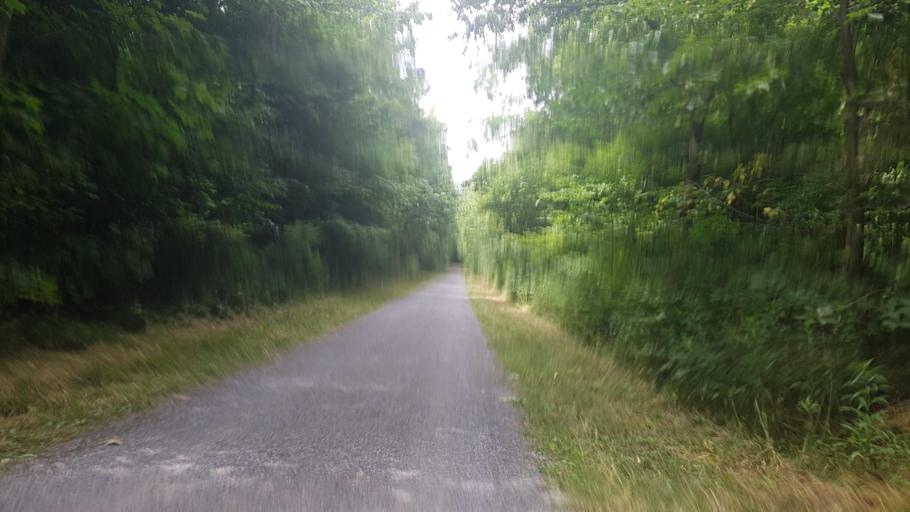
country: DE
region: Baden-Wuerttemberg
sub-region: Karlsruhe Region
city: Rheinstetten
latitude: 48.9762
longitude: 8.3535
